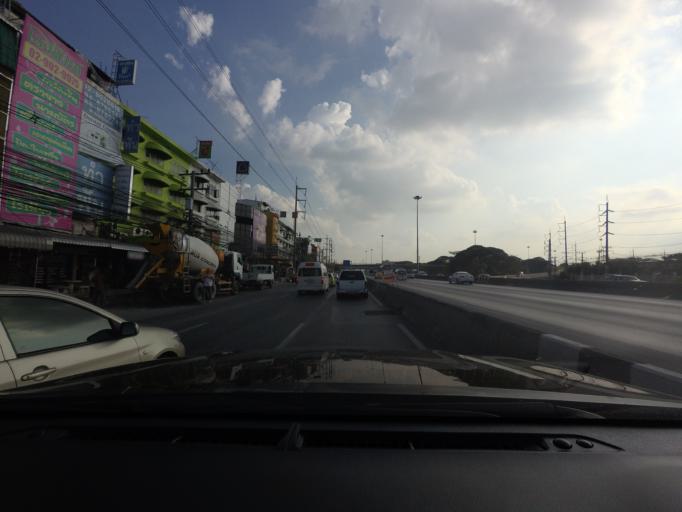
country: TH
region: Pathum Thani
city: Khlong Luang
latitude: 14.0670
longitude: 100.6177
